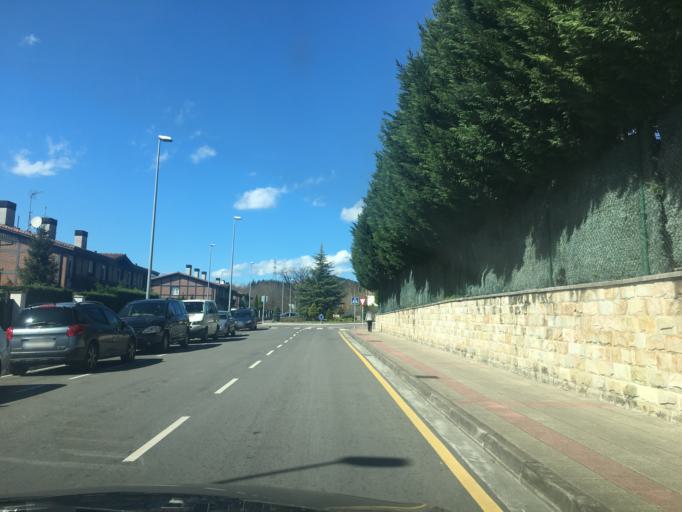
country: ES
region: Basque Country
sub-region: Bizkaia
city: Amorebieta
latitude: 43.2301
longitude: -2.7382
